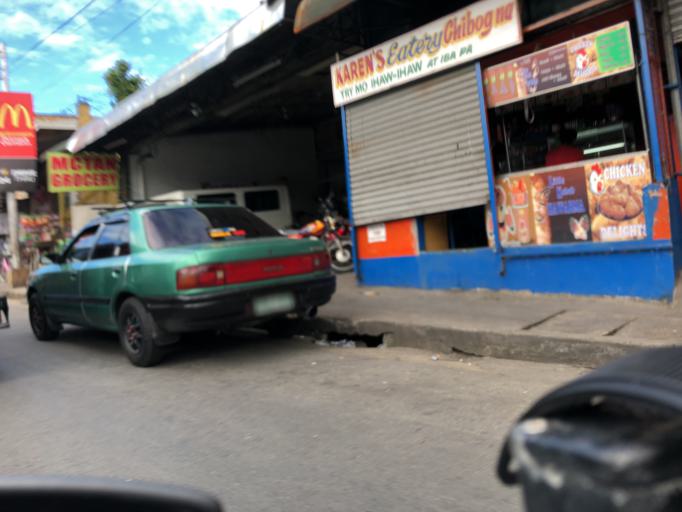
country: PH
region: Central Luzon
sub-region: Province of Bulacan
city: San Jose del Monte
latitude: 14.7423
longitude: 121.0566
